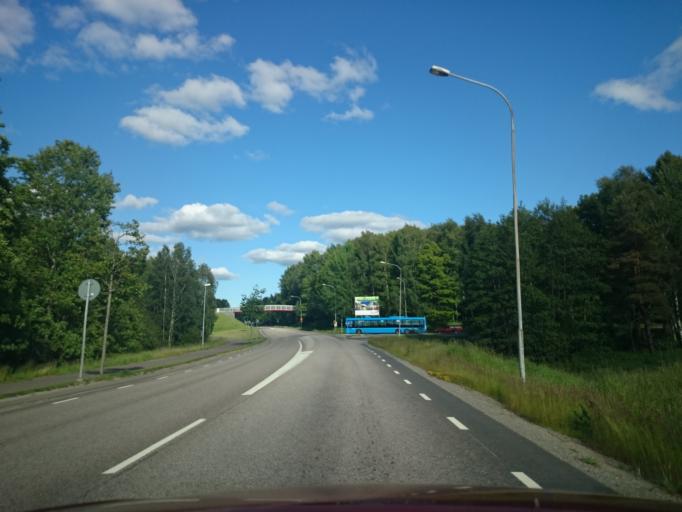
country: SE
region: Vaestra Goetaland
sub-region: Harryda Kommun
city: Molnlycke
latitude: 57.6677
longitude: 12.1009
